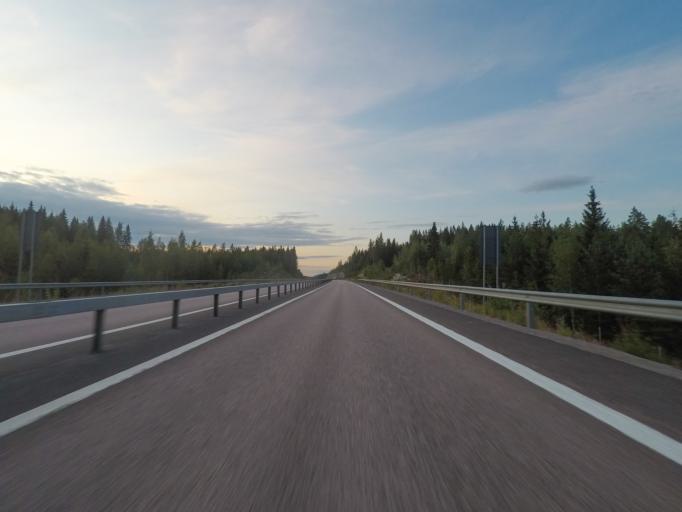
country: FI
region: Central Finland
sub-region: Jyvaeskylae
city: Saeynaetsalo
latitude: 62.1776
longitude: 25.9066
